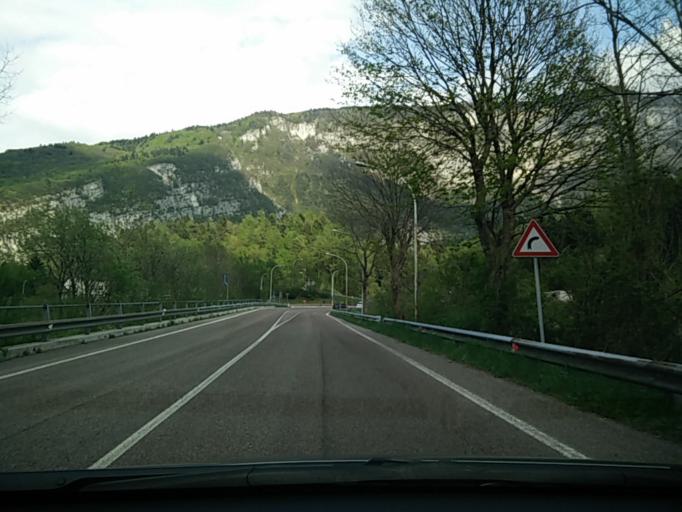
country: IT
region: Veneto
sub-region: Provincia di Belluno
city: Farra d'Alpago
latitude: 46.0857
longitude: 12.3354
